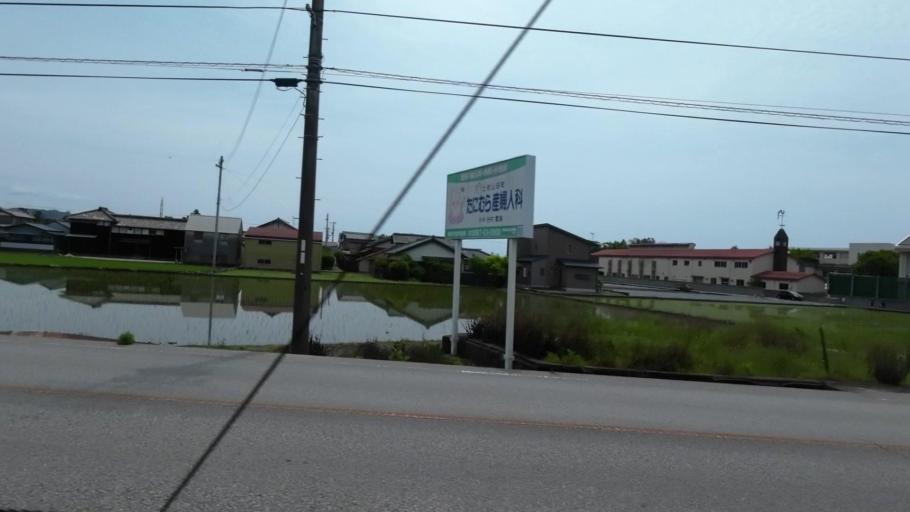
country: JP
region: Kochi
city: Kochi-shi
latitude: 33.5822
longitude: 133.6510
